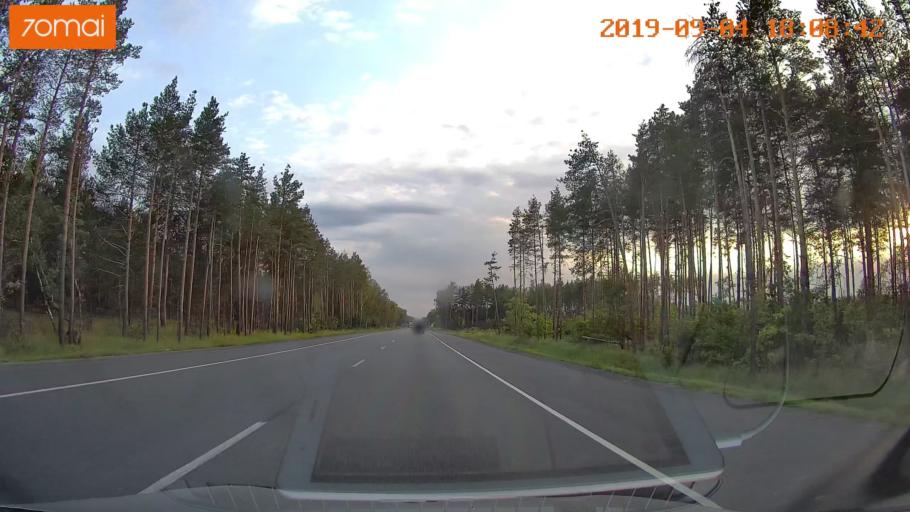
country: RU
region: Moskovskaya
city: Khorlovo
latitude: 55.4028
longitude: 38.7824
